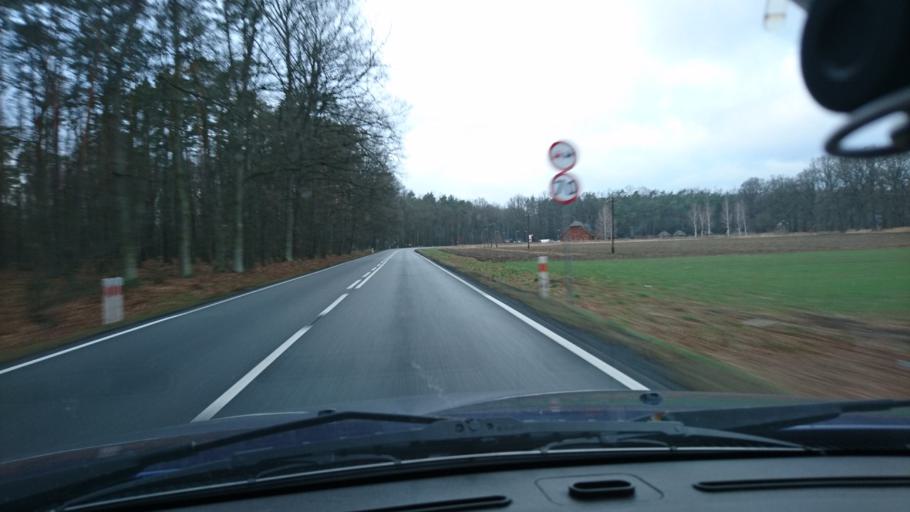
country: PL
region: Opole Voivodeship
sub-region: Powiat oleski
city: Olesno
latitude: 50.9197
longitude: 18.3414
